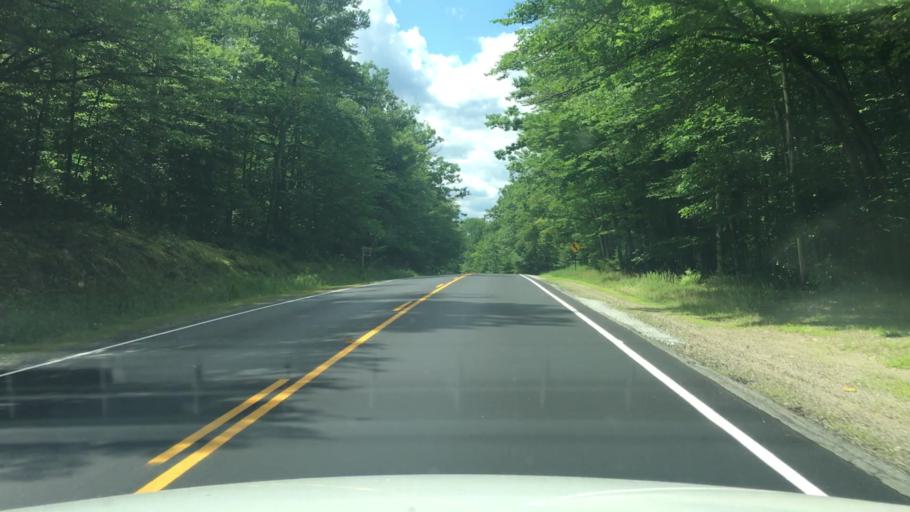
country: US
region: Maine
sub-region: Oxford County
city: West Paris
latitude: 44.3967
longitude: -70.6690
